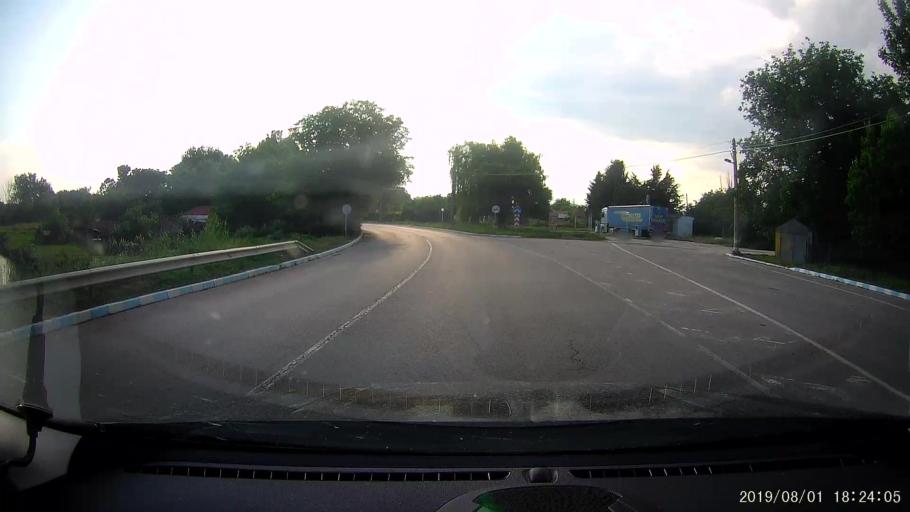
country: BG
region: Shumen
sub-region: Obshtina Kaolinovo
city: Kaolinovo
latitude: 43.6265
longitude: 27.0117
